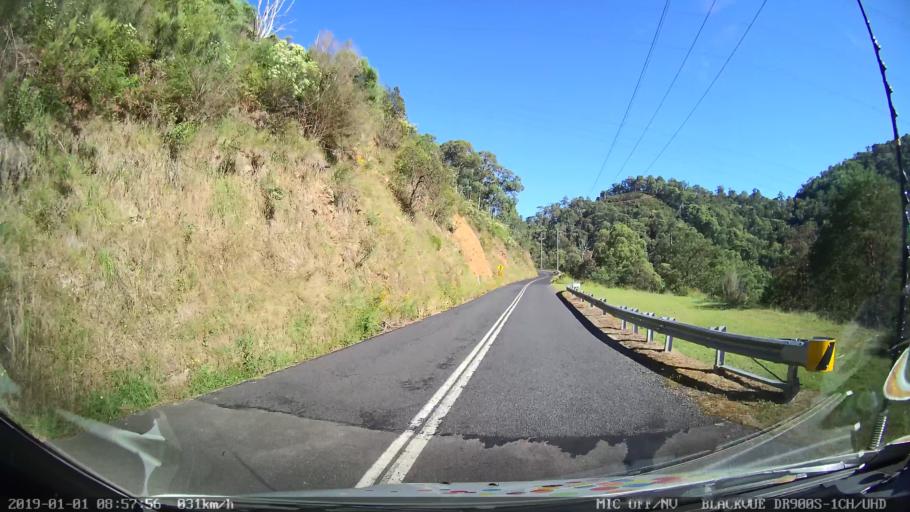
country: AU
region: New South Wales
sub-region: Snowy River
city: Jindabyne
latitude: -36.2468
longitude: 148.1883
